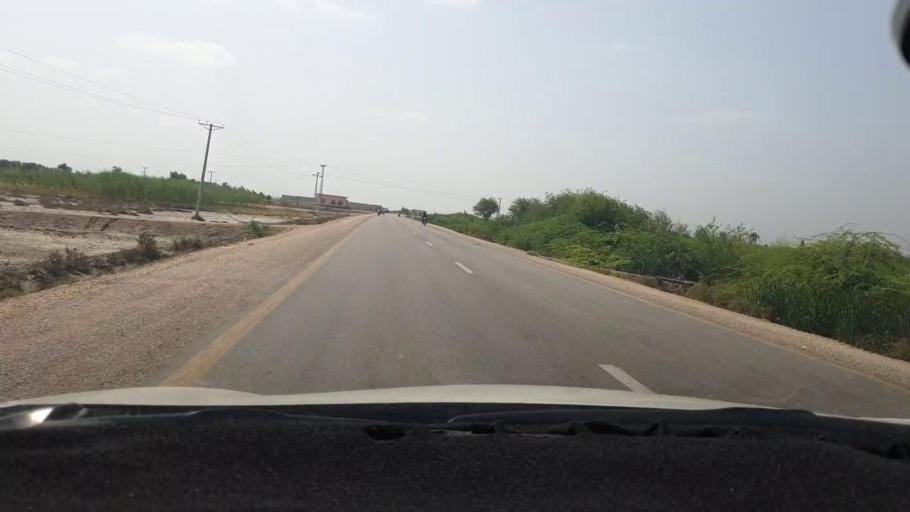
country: PK
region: Sindh
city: Mirpur Khas
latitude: 25.6000
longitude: 69.0835
